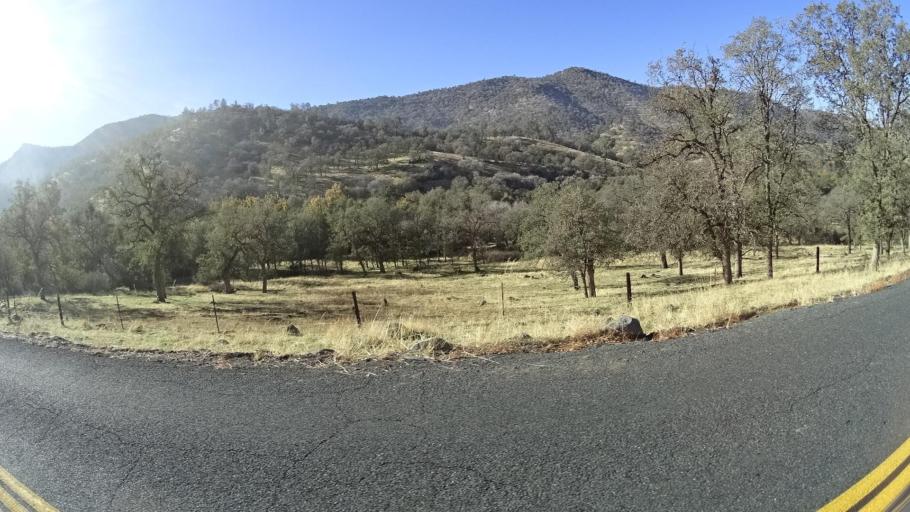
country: US
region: California
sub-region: Kern County
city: Alta Sierra
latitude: 35.7858
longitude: -118.7845
